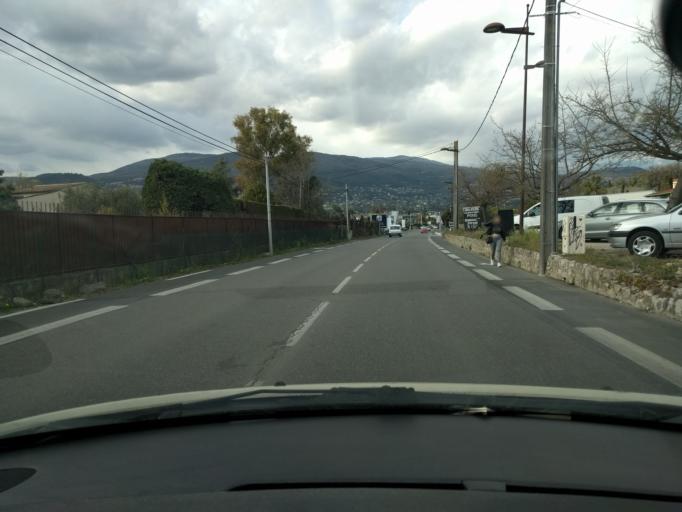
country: FR
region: Provence-Alpes-Cote d'Azur
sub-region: Departement des Alpes-Maritimes
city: Mouans-Sartoux
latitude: 43.6345
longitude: 6.9571
